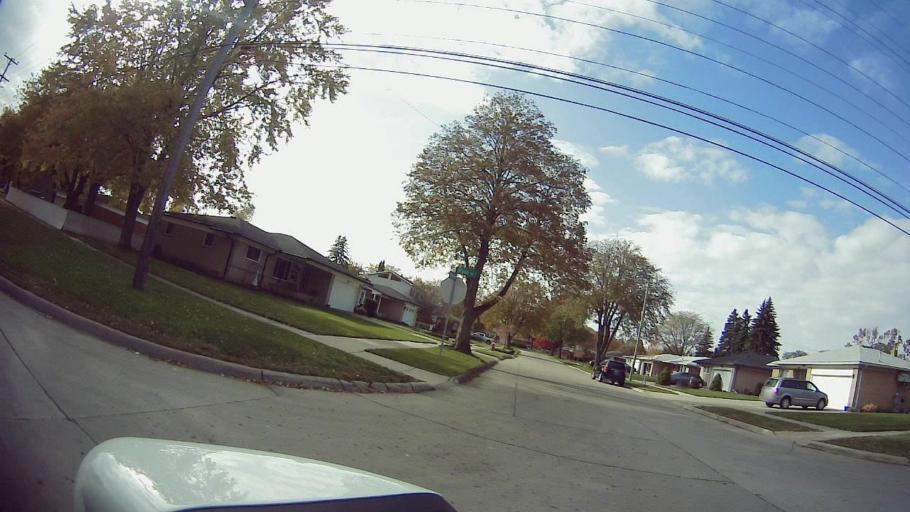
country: US
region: Michigan
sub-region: Oakland County
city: Madison Heights
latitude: 42.5012
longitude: -83.0674
